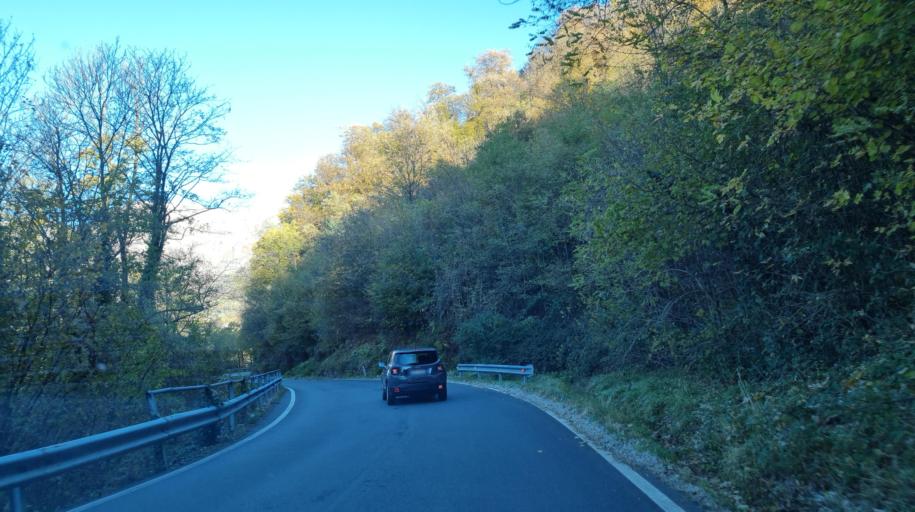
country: IT
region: Piedmont
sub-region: Provincia di Torino
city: Meugliano
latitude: 45.4780
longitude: 7.7826
